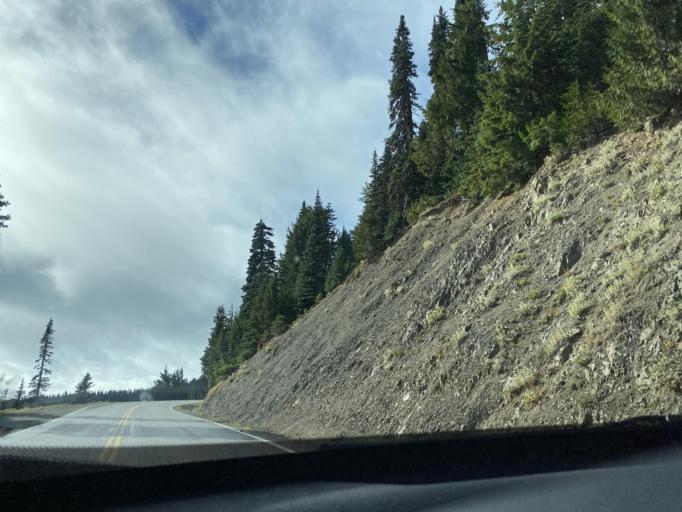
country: US
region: Washington
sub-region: Clallam County
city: Port Angeles
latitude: 47.9823
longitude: -123.4683
